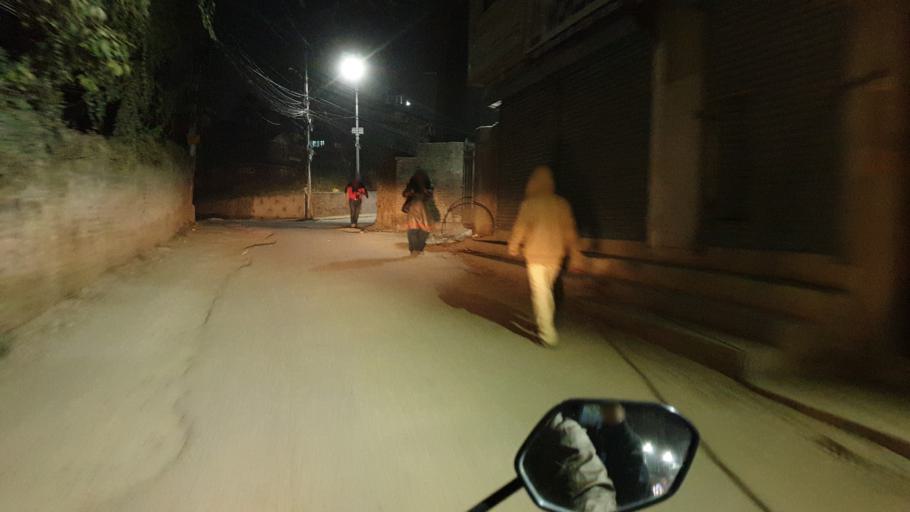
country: NP
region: Central Region
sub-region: Bagmati Zone
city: Kathmandu
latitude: 27.7001
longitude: 85.3077
